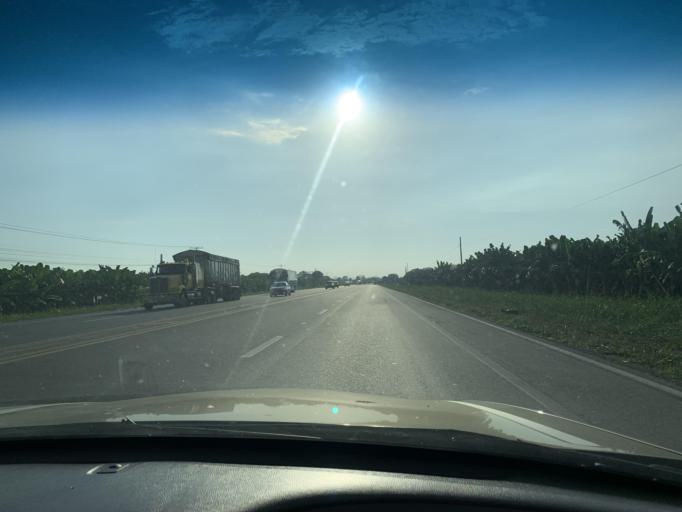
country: EC
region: Guayas
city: Yaguachi Nuevo
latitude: -2.2545
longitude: -79.6195
